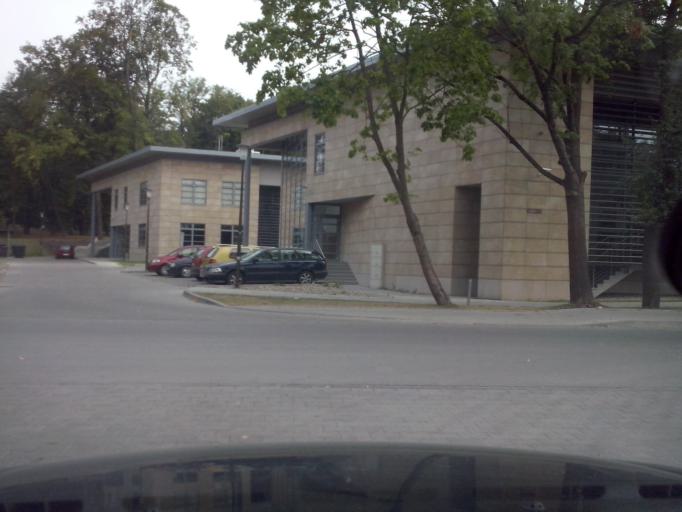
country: PL
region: Swietokrzyskie
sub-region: Powiat kielecki
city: Morawica
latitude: 50.7494
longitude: 20.6191
